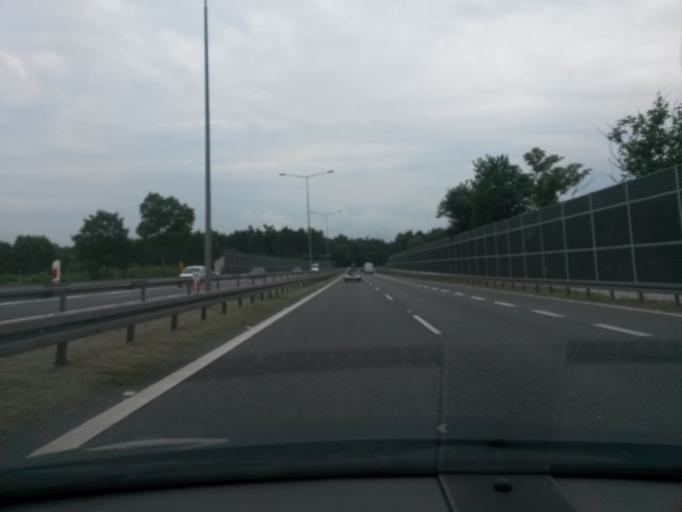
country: PL
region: Masovian Voivodeship
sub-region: Powiat zyrardowski
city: Mszczonow
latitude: 51.9350
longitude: 20.4759
